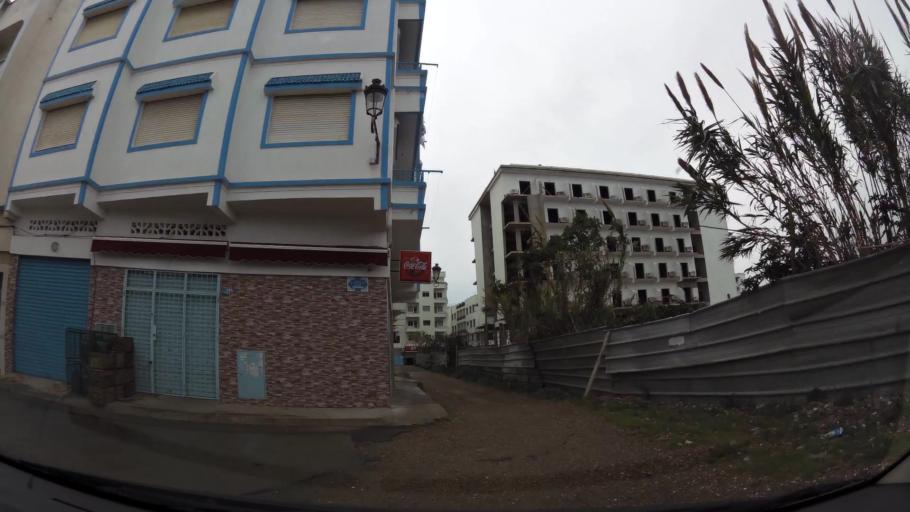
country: MA
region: Tanger-Tetouan
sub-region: Tetouan
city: Martil
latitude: 35.6139
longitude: -5.2857
